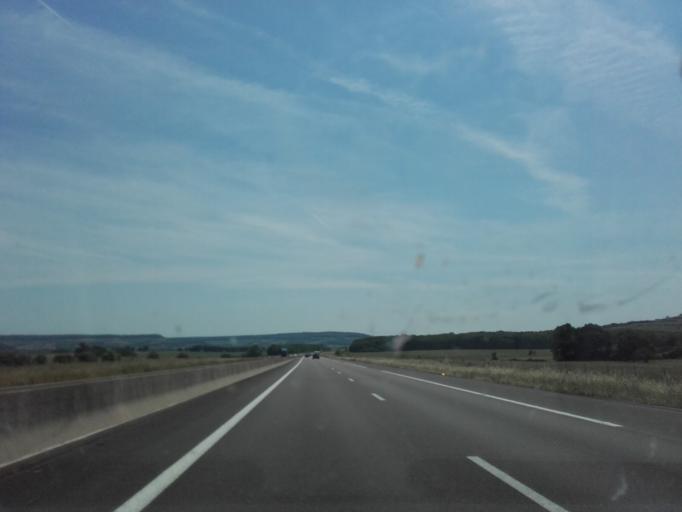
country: FR
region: Bourgogne
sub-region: Departement de la Cote-d'Or
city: Vitteaux
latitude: 47.3558
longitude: 4.4363
